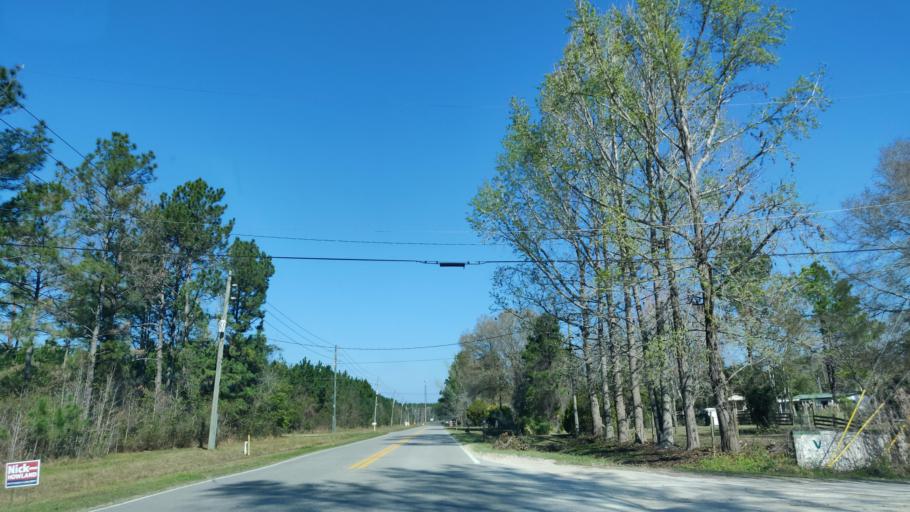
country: US
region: Florida
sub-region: Duval County
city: Baldwin
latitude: 30.2829
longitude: -81.9639
